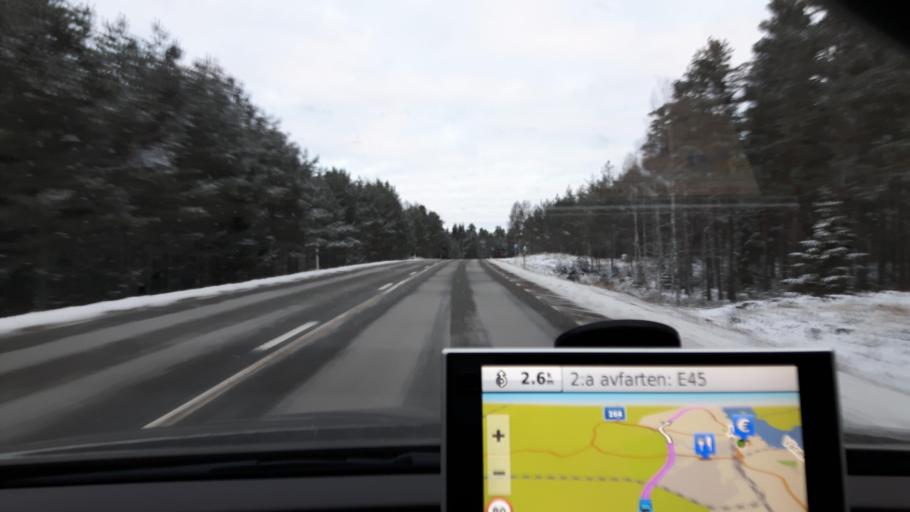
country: SE
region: Vaestra Goetaland
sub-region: Amals Kommun
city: Amal
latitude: 59.0323
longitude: 12.6712
